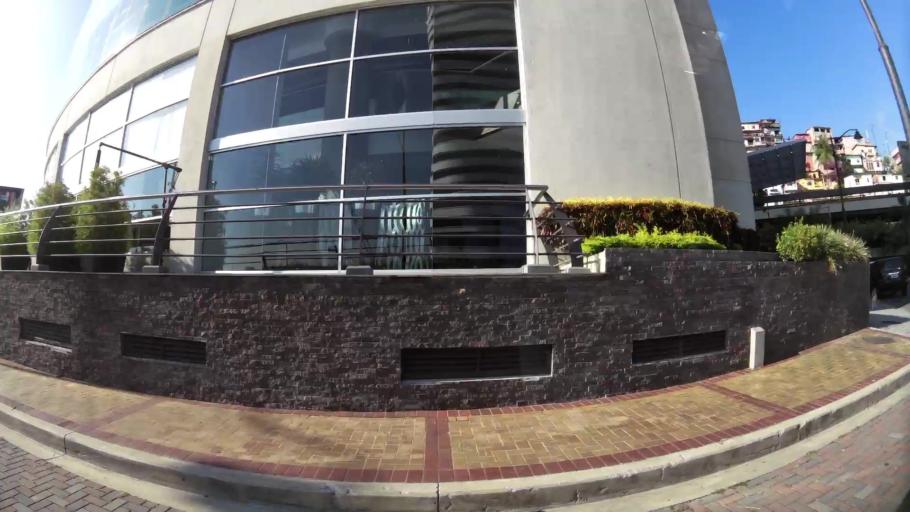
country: EC
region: Guayas
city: Eloy Alfaro
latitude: -2.1791
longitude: -79.8760
